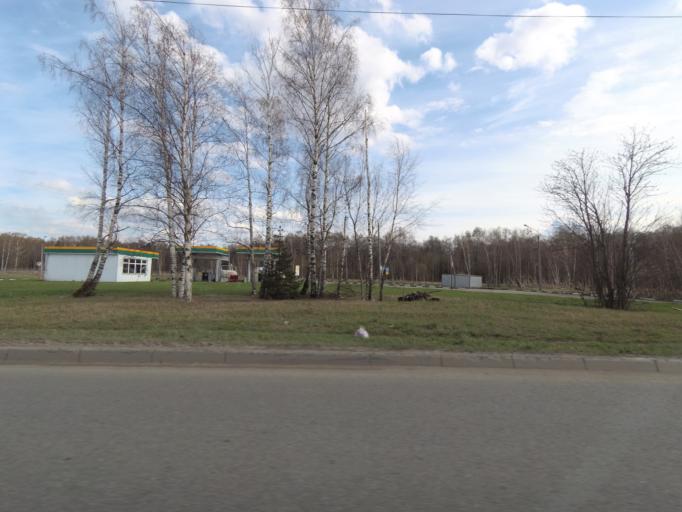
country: RU
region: Moskovskaya
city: Lobnya
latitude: 56.0000
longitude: 37.4244
